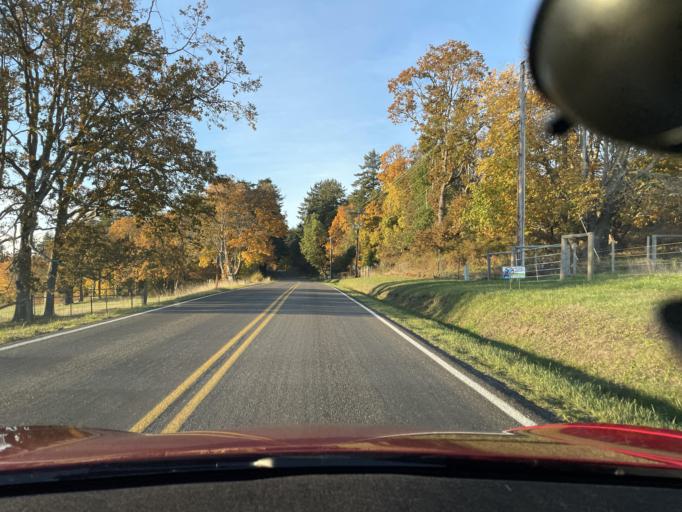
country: US
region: Washington
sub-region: San Juan County
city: Friday Harbor
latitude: 48.5774
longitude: -123.1417
